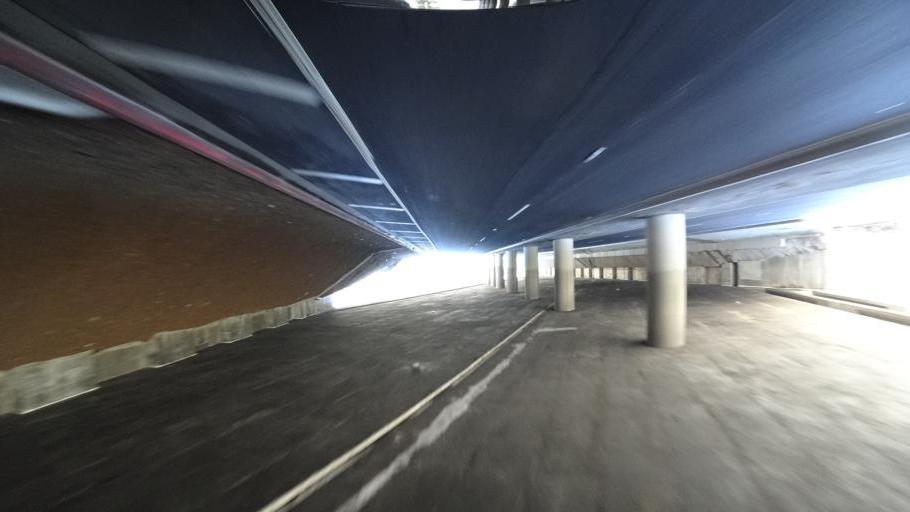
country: US
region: California
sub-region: Los Angeles County
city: Rowland Heights
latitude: 33.9579
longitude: -117.8598
